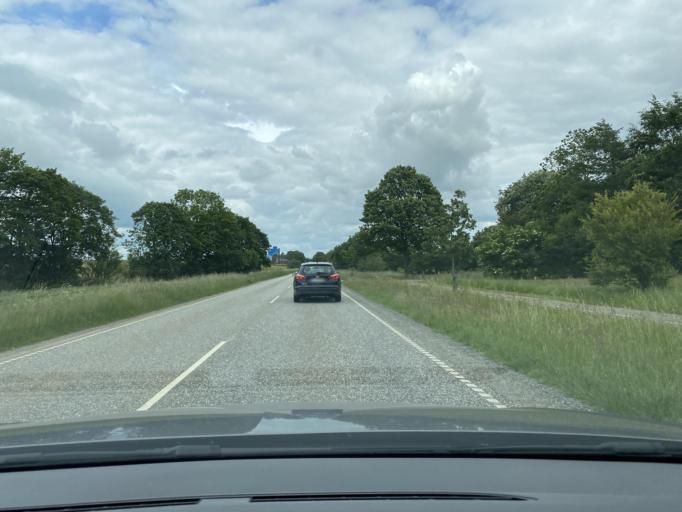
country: DK
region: South Denmark
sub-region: Vejle Kommune
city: Jelling
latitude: 55.6680
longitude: 9.4198
